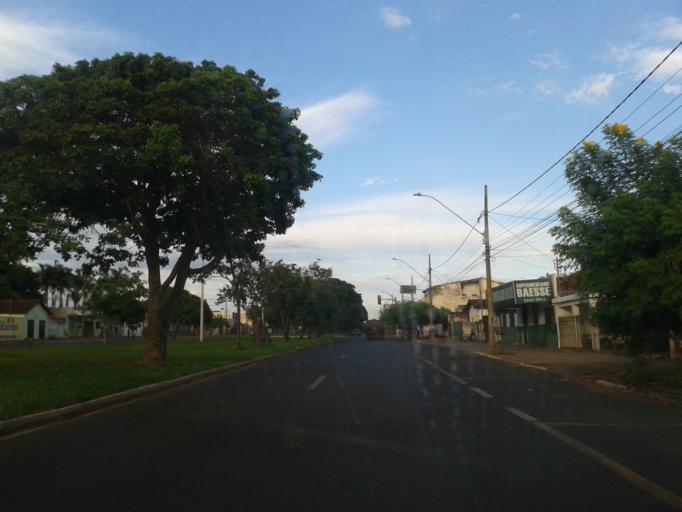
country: BR
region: Minas Gerais
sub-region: Araguari
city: Araguari
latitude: -18.6407
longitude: -48.1993
